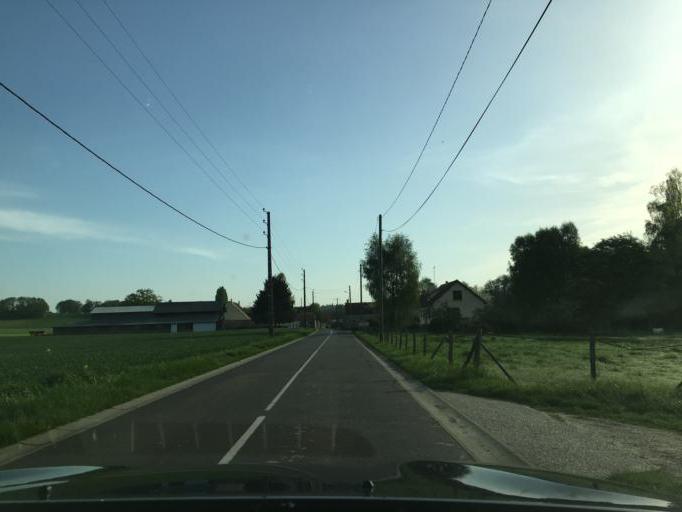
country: FR
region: Centre
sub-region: Departement d'Eure-et-Loir
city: Epernon
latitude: 48.6438
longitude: 1.6811
